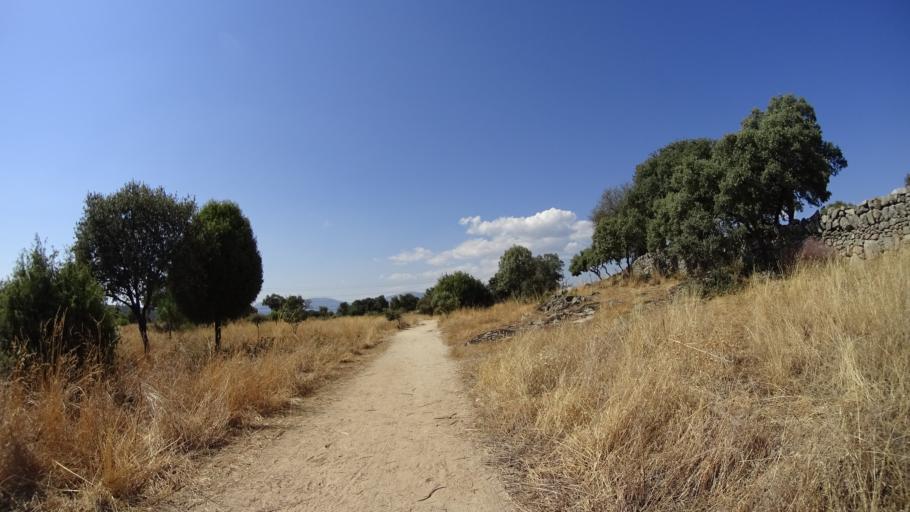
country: ES
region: Madrid
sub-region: Provincia de Madrid
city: Galapagar
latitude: 40.5999
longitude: -4.0113
